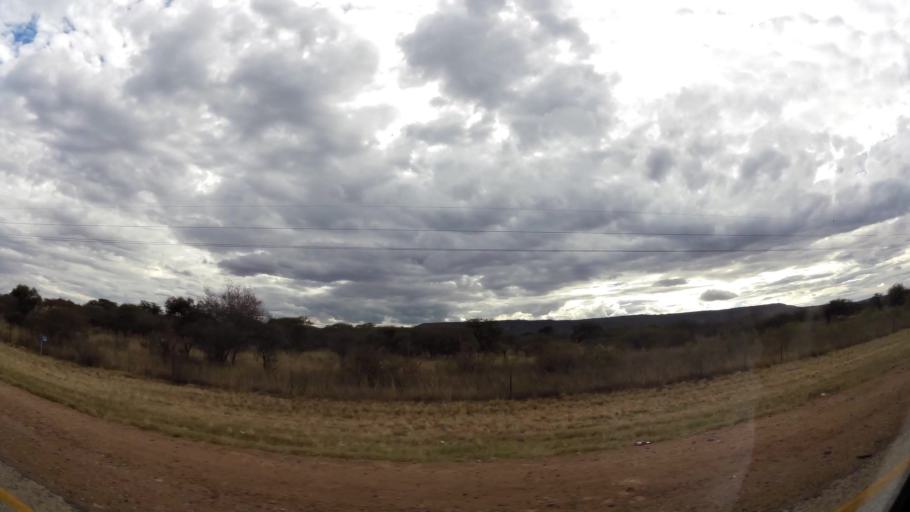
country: ZA
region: Limpopo
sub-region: Waterberg District Municipality
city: Modimolle
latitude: -24.5601
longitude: 28.6835
